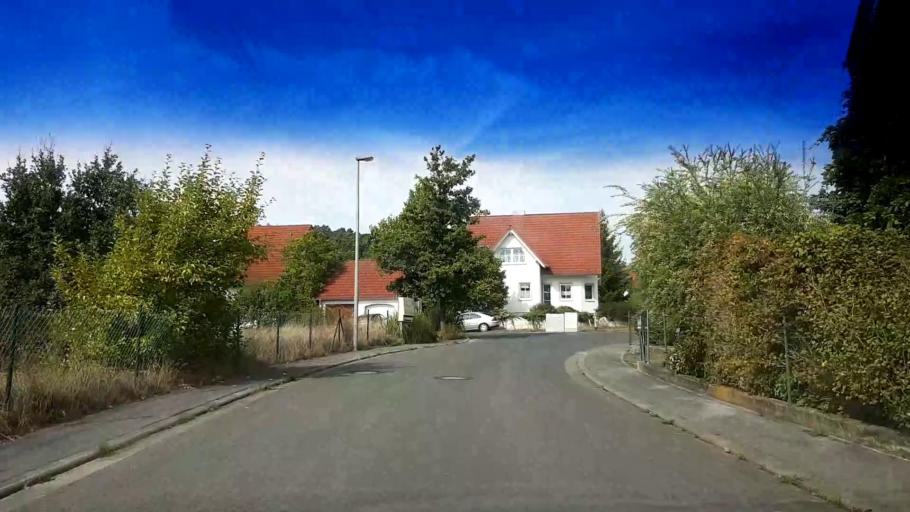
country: DE
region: Bavaria
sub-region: Upper Franconia
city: Oberhaid
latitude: 49.9374
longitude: 10.8062
